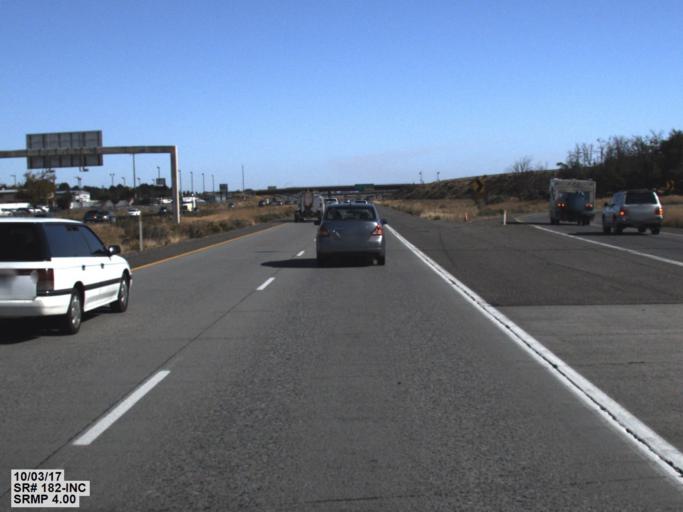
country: US
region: Washington
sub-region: Benton County
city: Richland
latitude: 46.2588
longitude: -119.2823
